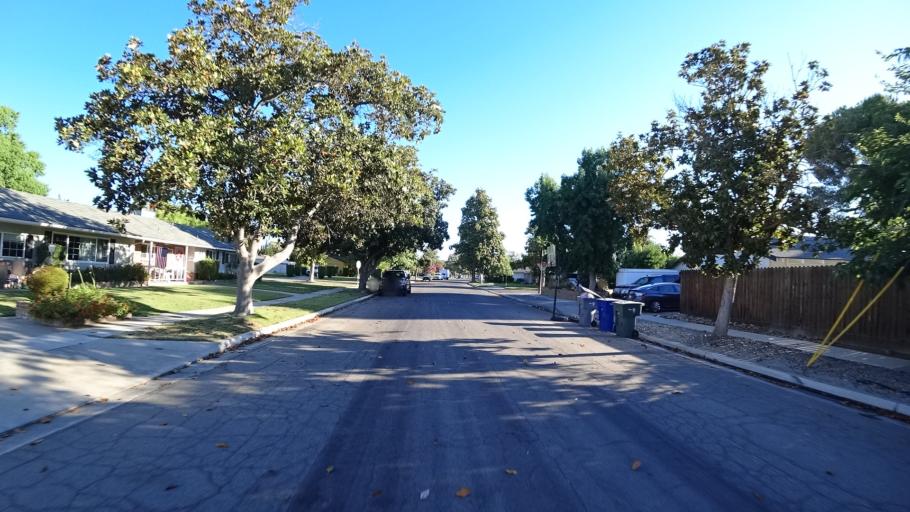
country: US
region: California
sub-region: Fresno County
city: Fresno
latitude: 36.8038
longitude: -119.8199
